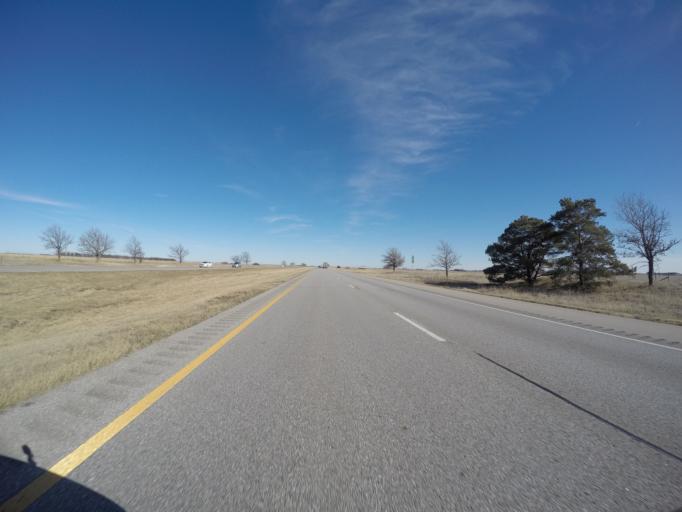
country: US
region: Nebraska
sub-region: Seward County
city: Seward
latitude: 40.8222
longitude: -97.1579
